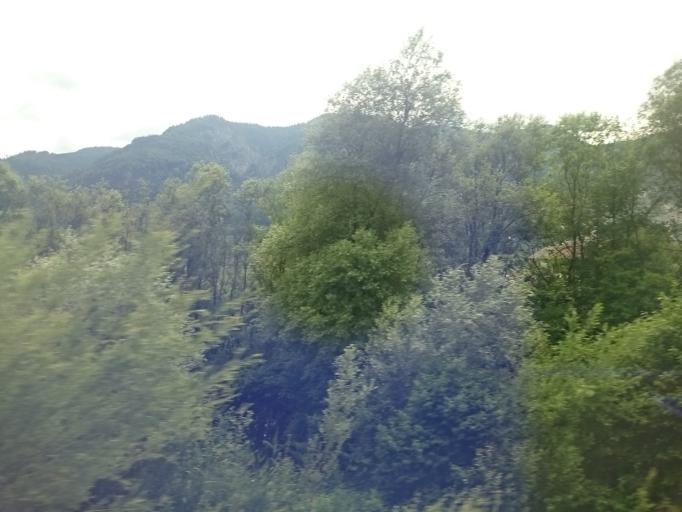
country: AT
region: Tyrol
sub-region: Politischer Bezirk Kufstein
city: Kundl
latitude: 47.4808
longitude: 12.0183
